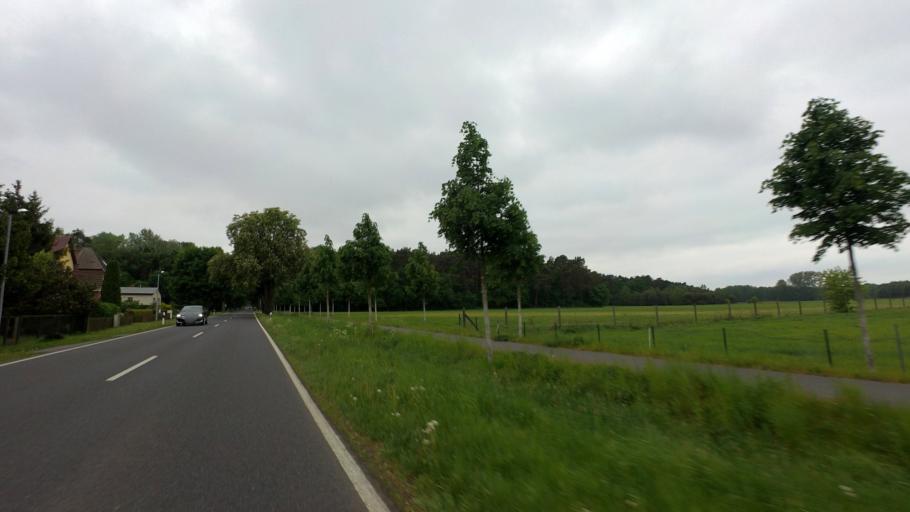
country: DE
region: Brandenburg
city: Wandlitz
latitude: 52.8085
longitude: 13.4921
